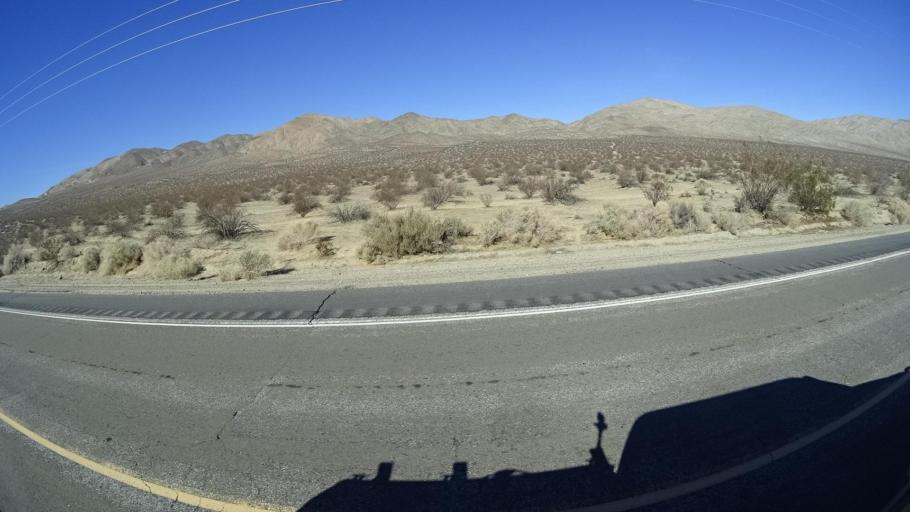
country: US
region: California
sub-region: Kern County
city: California City
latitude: 35.3466
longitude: -117.9257
